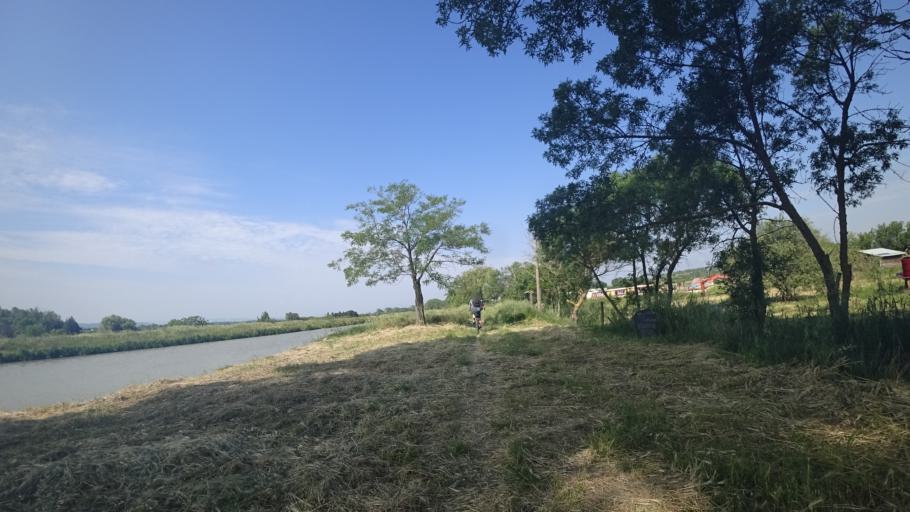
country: FR
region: Languedoc-Roussillon
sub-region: Departement de l'Aude
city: Ginestas
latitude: 43.2577
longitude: 2.8957
